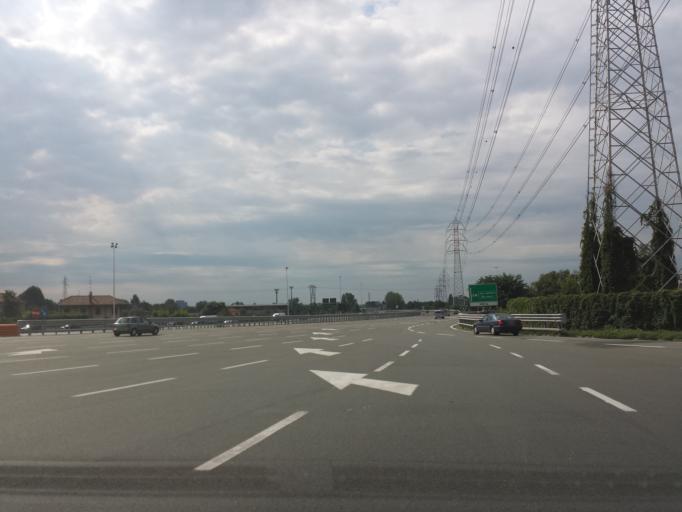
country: IT
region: Lombardy
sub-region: Citta metropolitana di Milano
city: Rho
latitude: 45.5405
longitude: 9.0579
